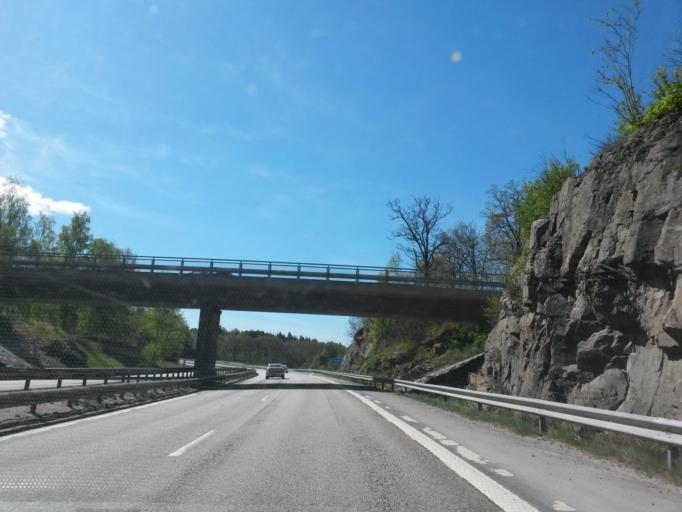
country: SE
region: Vaestra Goetaland
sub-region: Alingsas Kommun
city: Alingsas
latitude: 57.8987
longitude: 12.4915
